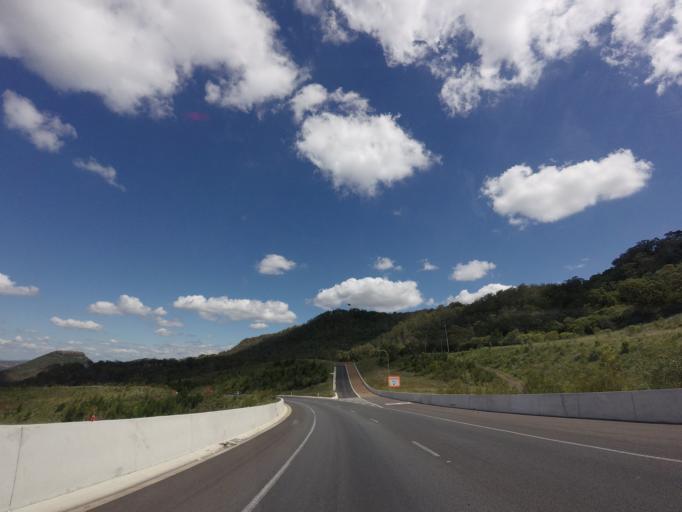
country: AU
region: Queensland
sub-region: Toowoomba
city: East Toowoomba
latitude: -27.5705
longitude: 151.9831
